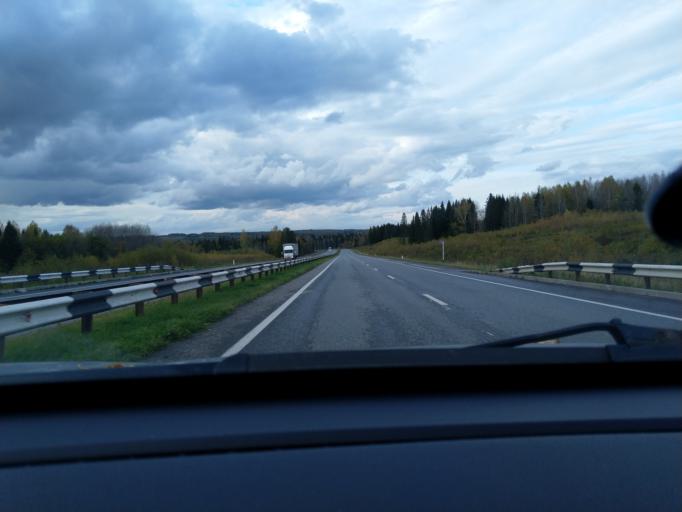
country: RU
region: Perm
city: Polazna
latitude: 58.3021
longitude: 56.4841
